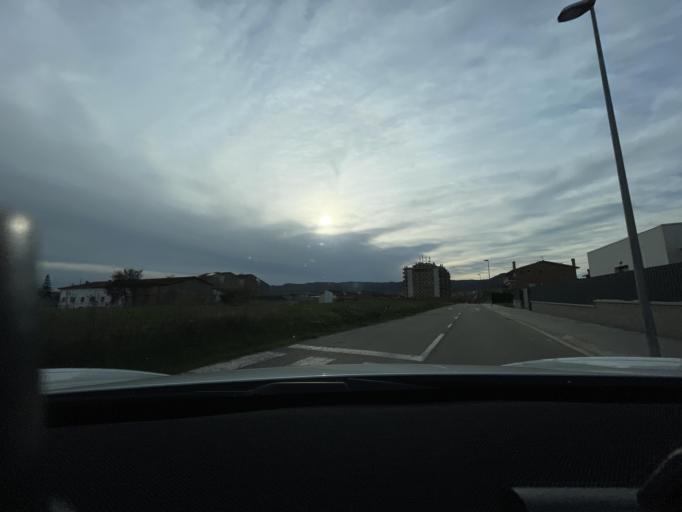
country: ES
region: Catalonia
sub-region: Provincia de Lleida
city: Solsona
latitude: 41.9956
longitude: 1.5291
